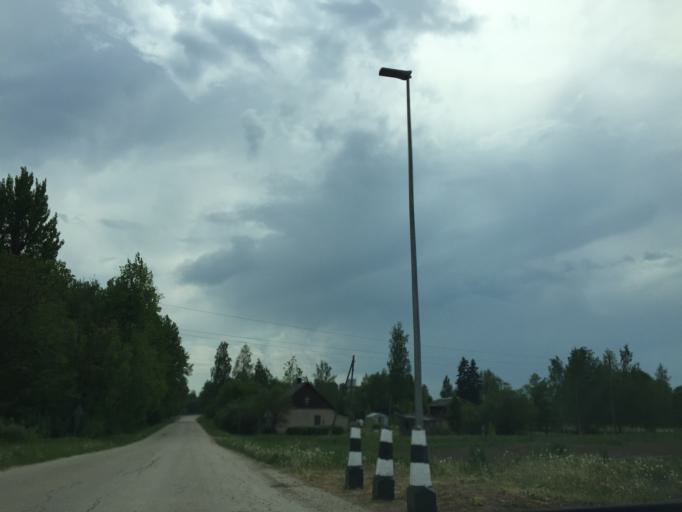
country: LV
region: Livani
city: Livani
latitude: 56.5416
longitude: 26.2446
